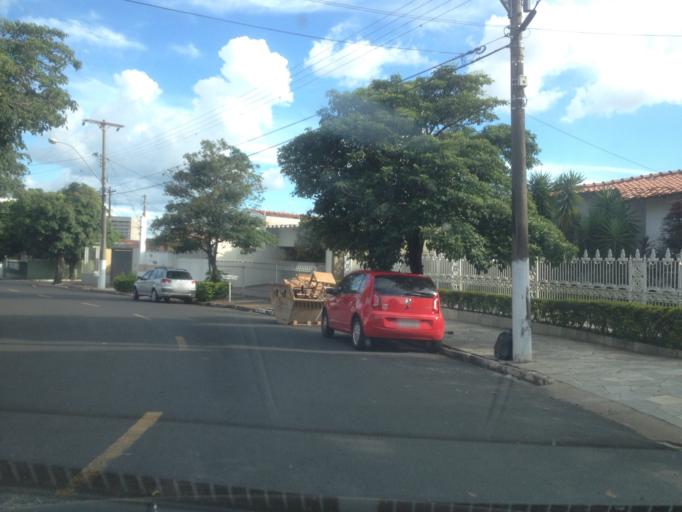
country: BR
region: Sao Paulo
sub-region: Marilia
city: Marilia
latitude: -22.2206
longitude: -49.9362
